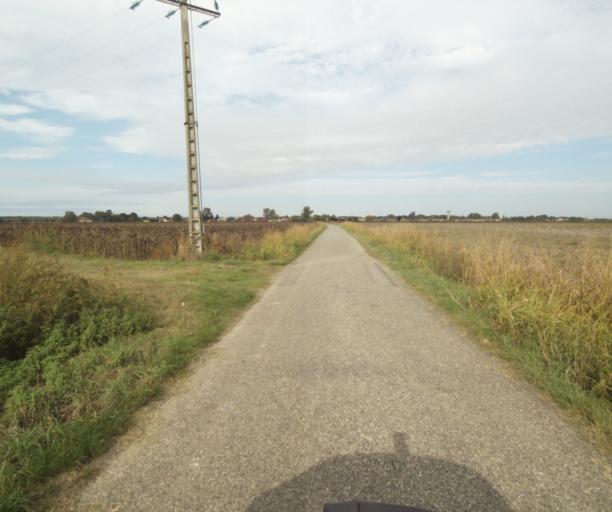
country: FR
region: Midi-Pyrenees
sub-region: Departement du Tarn-et-Garonne
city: Finhan
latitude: 43.9048
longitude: 1.2347
